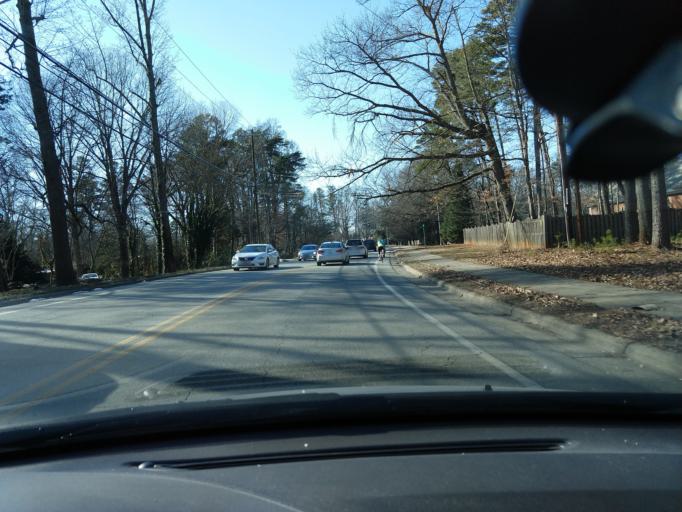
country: US
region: North Carolina
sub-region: Guilford County
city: Greensboro
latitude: 36.1162
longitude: -79.8480
